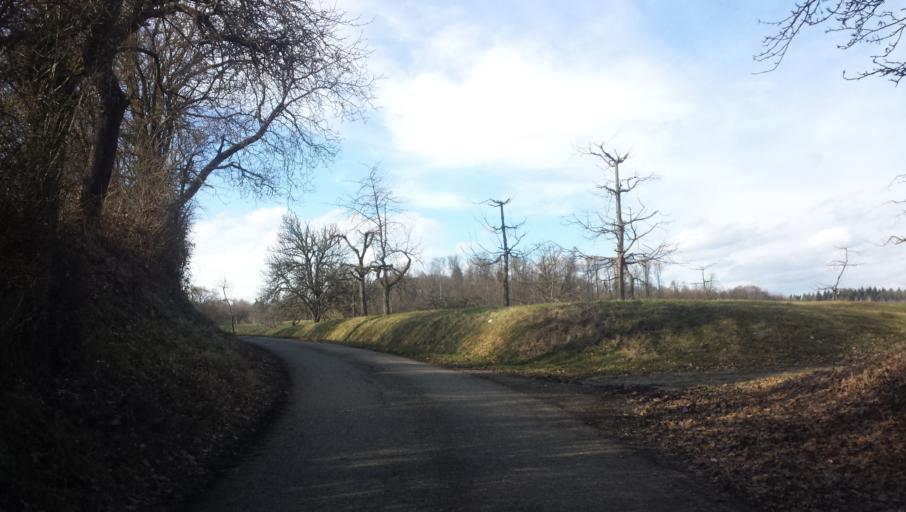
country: DE
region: Baden-Wuerttemberg
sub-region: Karlsruhe Region
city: Meckesheim
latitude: 49.3399
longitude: 8.8419
